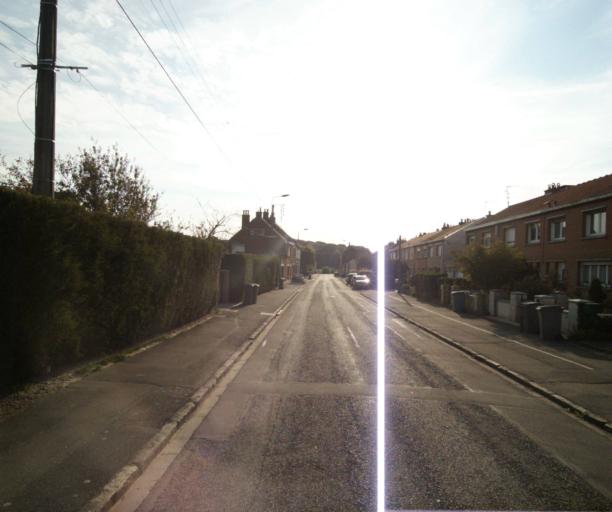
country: FR
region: Nord-Pas-de-Calais
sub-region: Departement du Nord
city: Lompret
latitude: 50.6618
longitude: 2.9819
